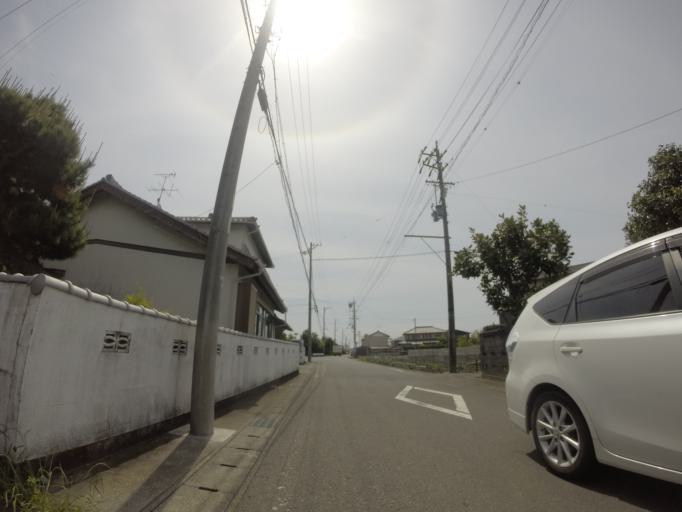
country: JP
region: Shizuoka
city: Fujieda
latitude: 34.8013
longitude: 138.2910
